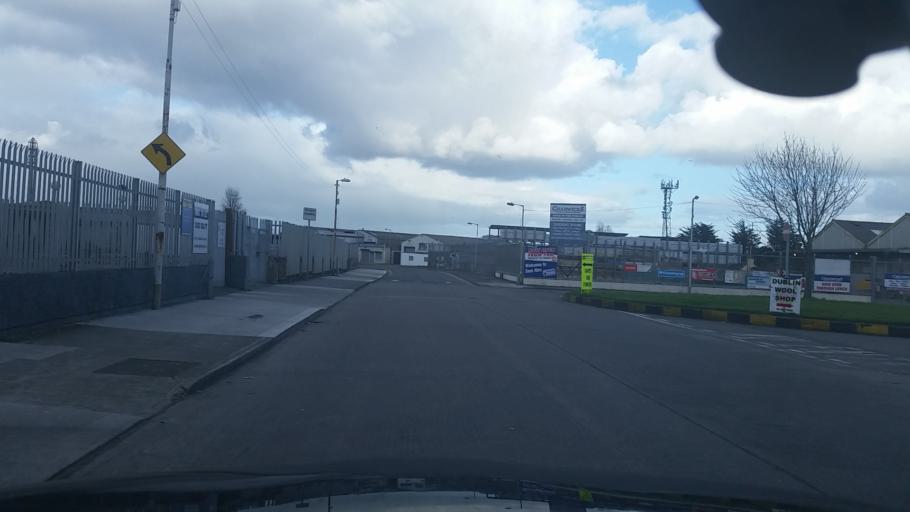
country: IE
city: Coolock
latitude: 53.3943
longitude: -6.1957
